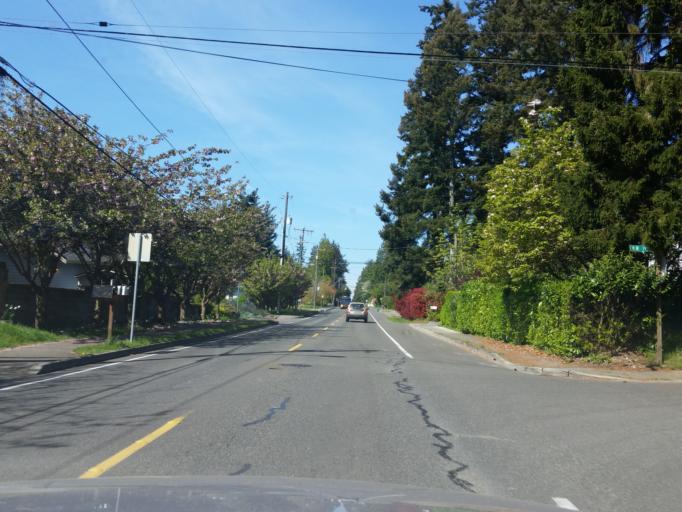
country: US
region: Washington
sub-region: Snohomish County
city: Esperance
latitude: 47.7685
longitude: -122.3612
